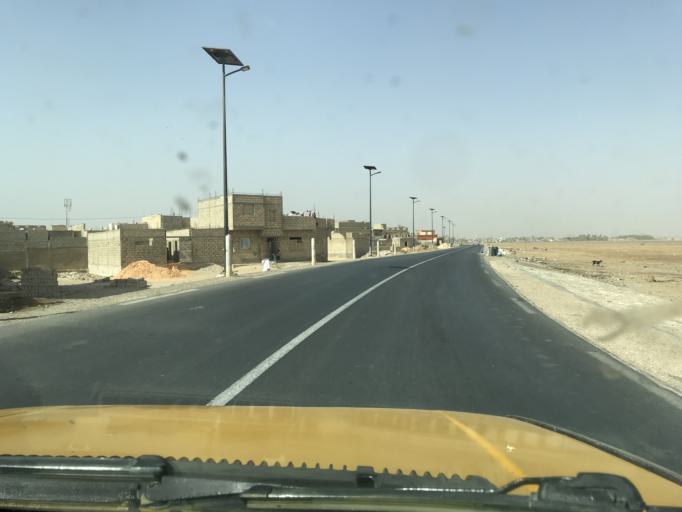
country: SN
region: Saint-Louis
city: Saint-Louis
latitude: 16.0143
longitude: -16.4849
